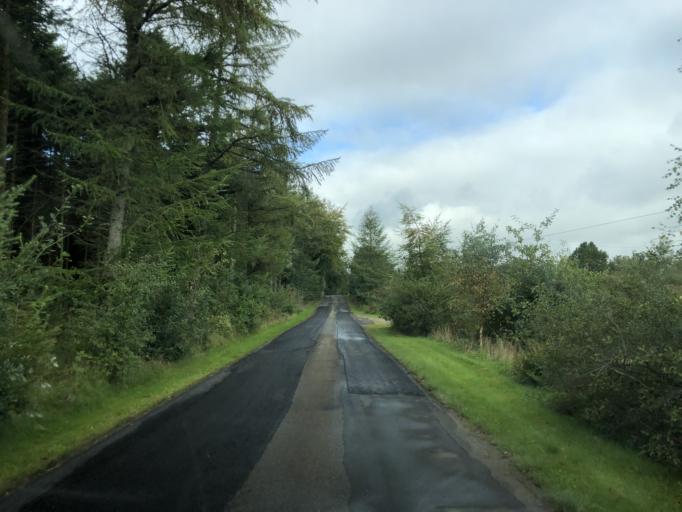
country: DK
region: Central Jutland
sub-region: Holstebro Kommune
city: Ulfborg
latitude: 56.3062
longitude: 8.4329
